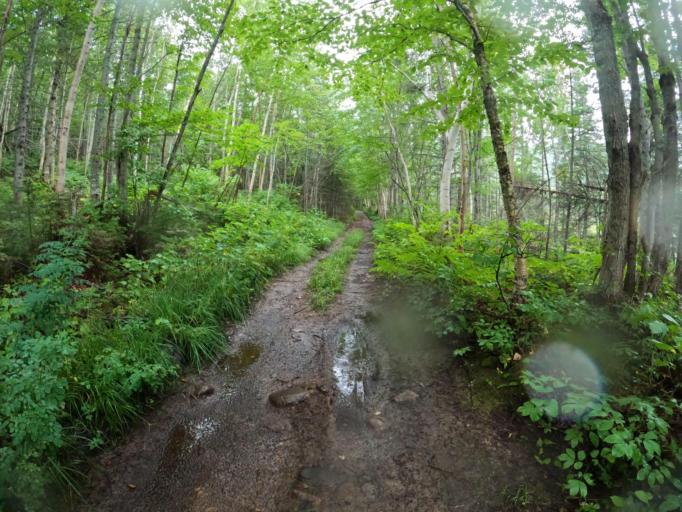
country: CA
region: Quebec
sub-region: Capitale-Nationale
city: La Malbaie
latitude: 47.8342
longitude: -70.4612
